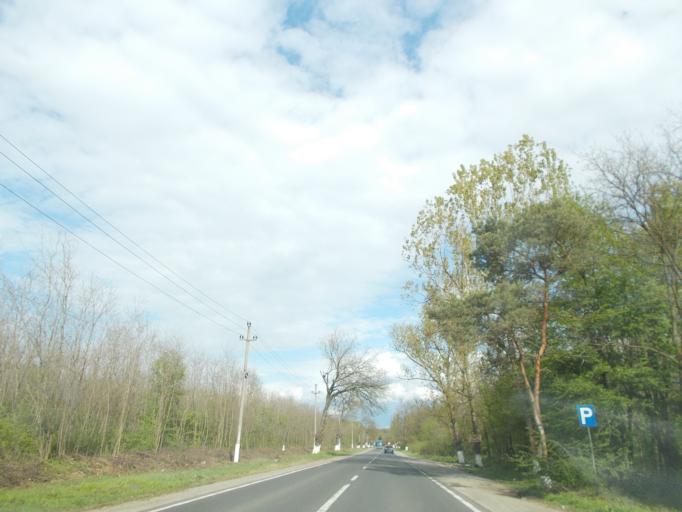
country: RO
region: Ilfov
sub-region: Comuna Ganeasa
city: Ganeasa
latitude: 44.4561
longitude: 26.2871
